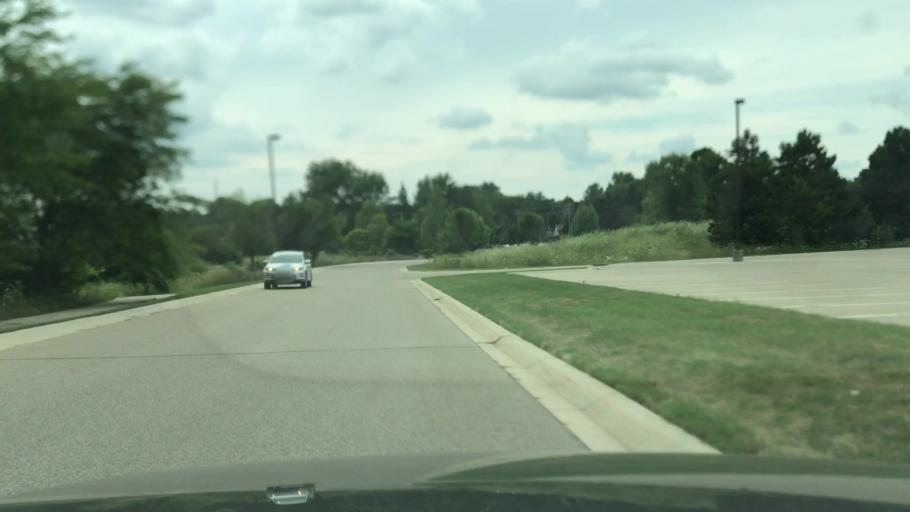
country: US
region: Michigan
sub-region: Kent County
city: East Grand Rapids
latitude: 42.9508
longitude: -85.5528
